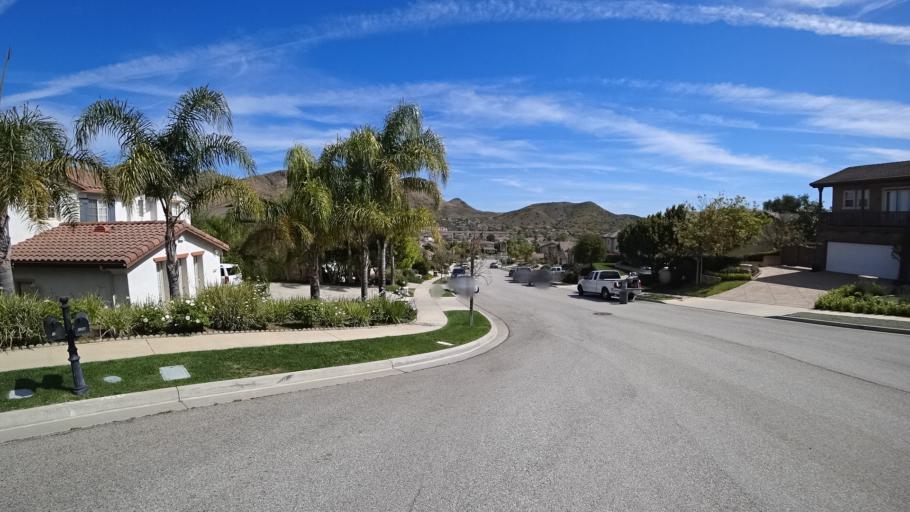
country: US
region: California
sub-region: Ventura County
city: Casa Conejo
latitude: 34.1702
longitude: -118.9798
